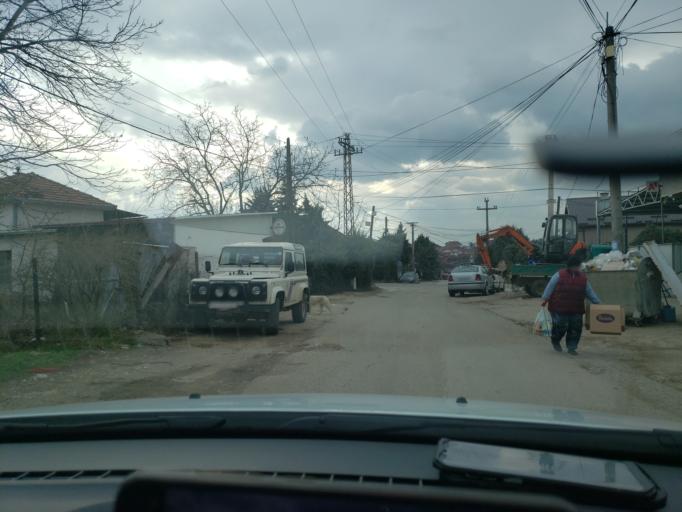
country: MK
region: Kumanovo
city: Kumanovo
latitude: 42.1452
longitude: 21.7418
